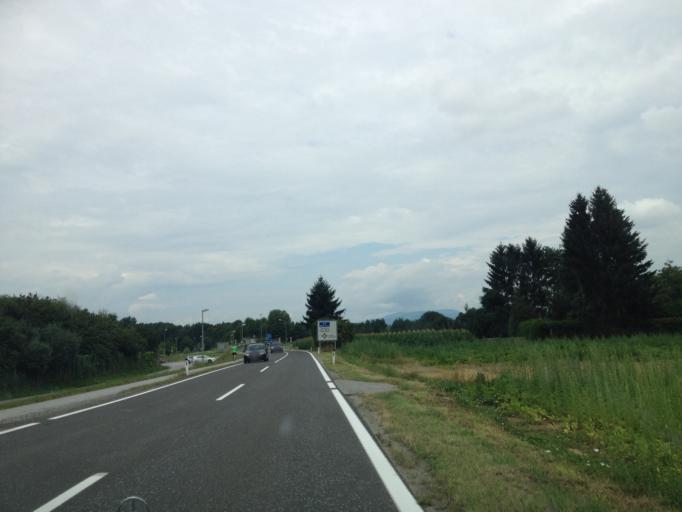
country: AT
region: Styria
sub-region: Politischer Bezirk Hartberg-Fuerstenfeld
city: Bad Waltersdorf
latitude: 47.1768
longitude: 16.0036
